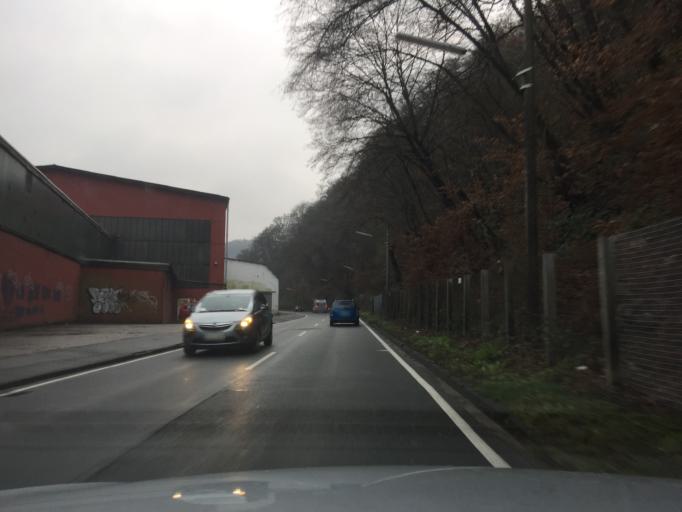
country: DE
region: North Rhine-Westphalia
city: Wetter (Ruhr)
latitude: 51.3811
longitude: 7.3818
